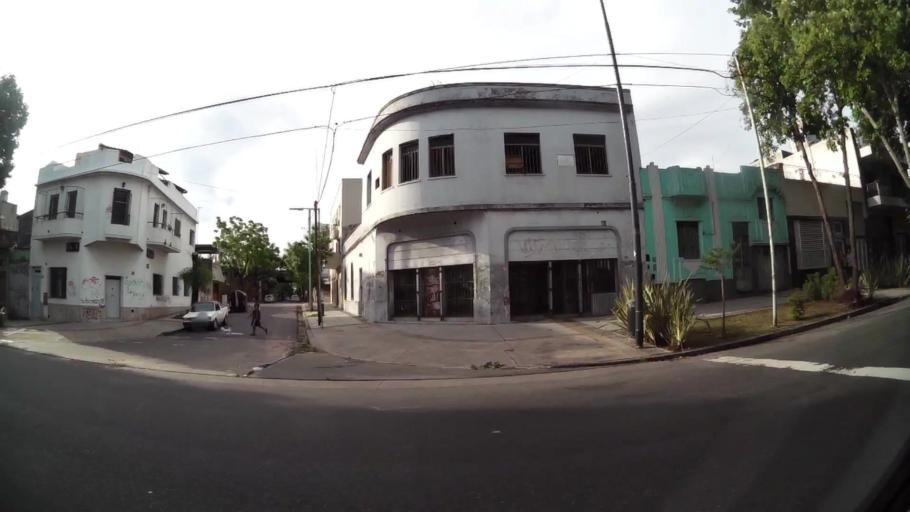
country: AR
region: Buenos Aires F.D.
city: Villa Santa Rita
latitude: -34.6420
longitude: -58.4587
